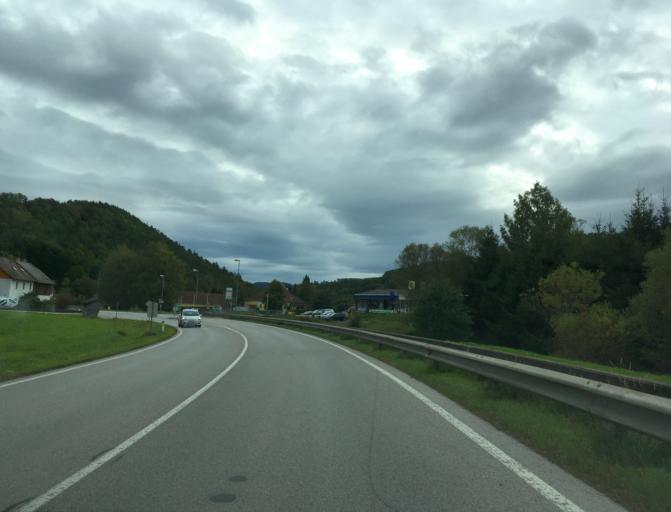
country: AT
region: Lower Austria
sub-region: Politischer Bezirk Wiener Neustadt
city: Bad Schonau
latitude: 47.5043
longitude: 16.2038
